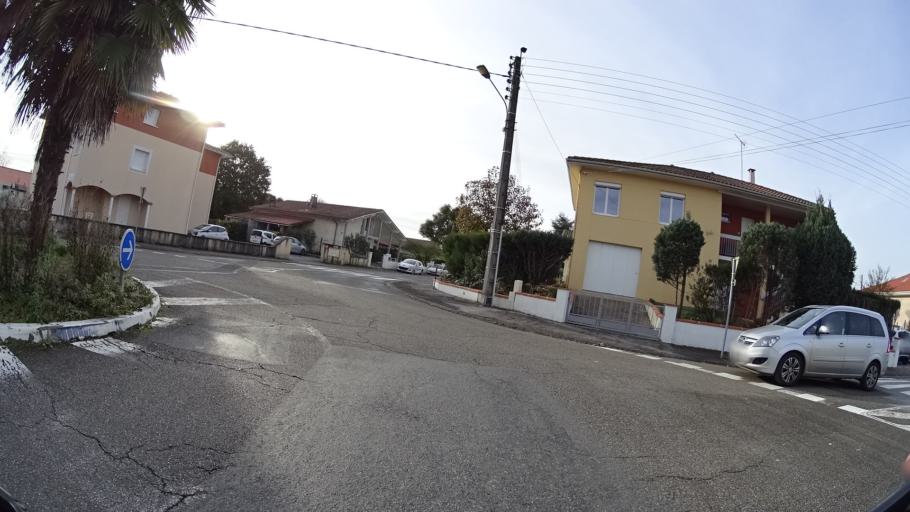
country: FR
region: Aquitaine
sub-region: Departement des Landes
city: Saint-Paul-les-Dax
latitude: 43.7293
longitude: -1.0518
